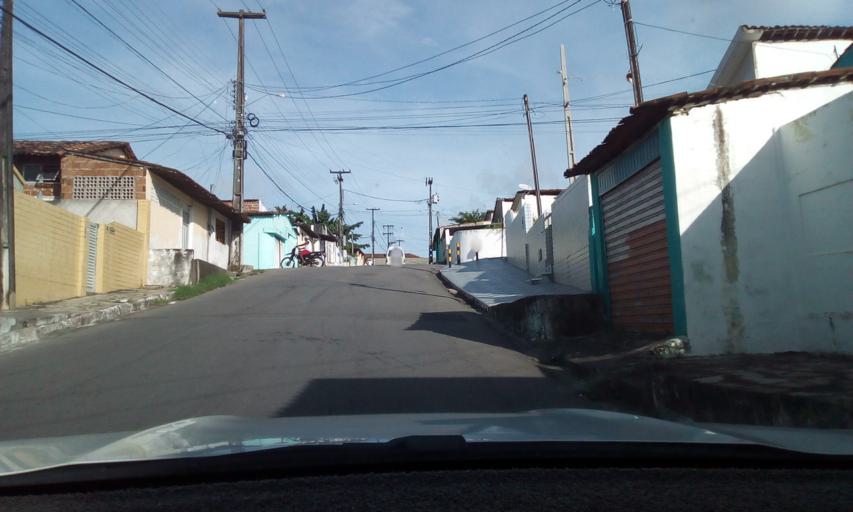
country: BR
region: Paraiba
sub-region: Joao Pessoa
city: Joao Pessoa
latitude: -7.1353
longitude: -34.8865
